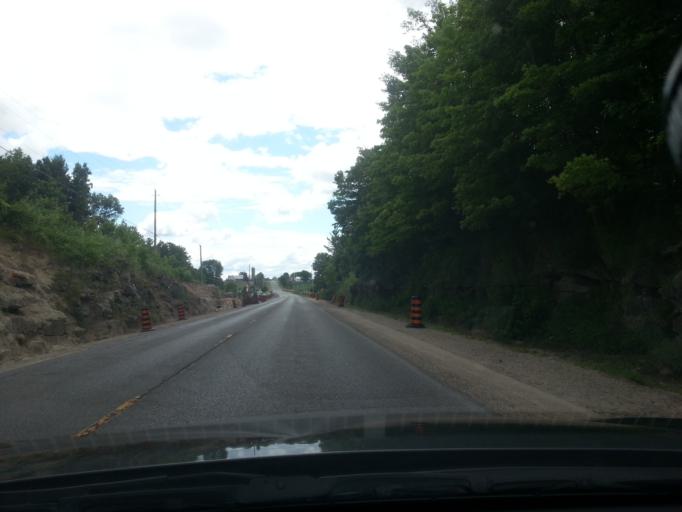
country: CA
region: Ontario
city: Perth
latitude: 44.6260
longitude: -76.2474
